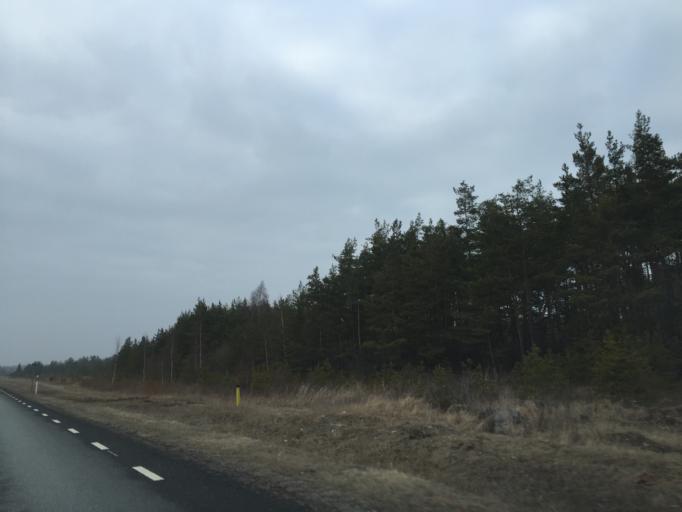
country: EE
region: Saare
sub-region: Orissaare vald
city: Orissaare
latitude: 58.5848
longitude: 23.3482
